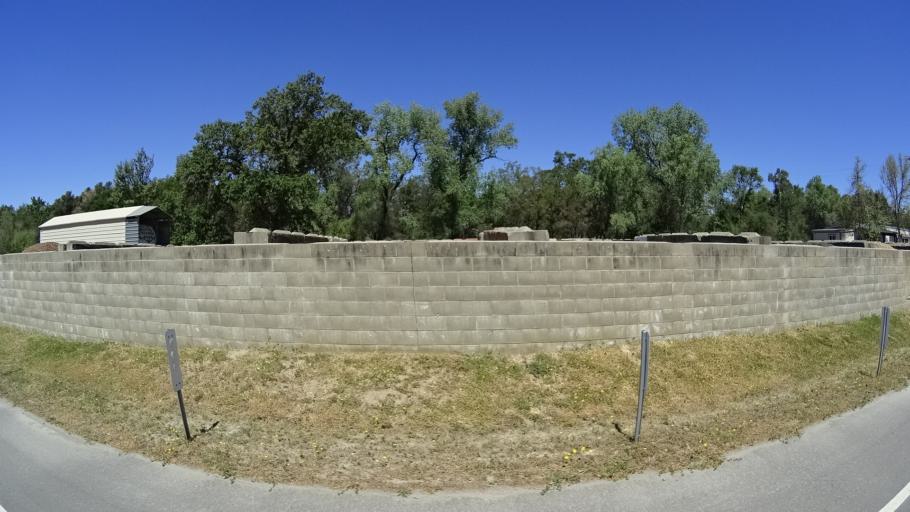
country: US
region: California
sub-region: Placer County
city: Loomis
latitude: 38.8097
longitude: -121.2099
